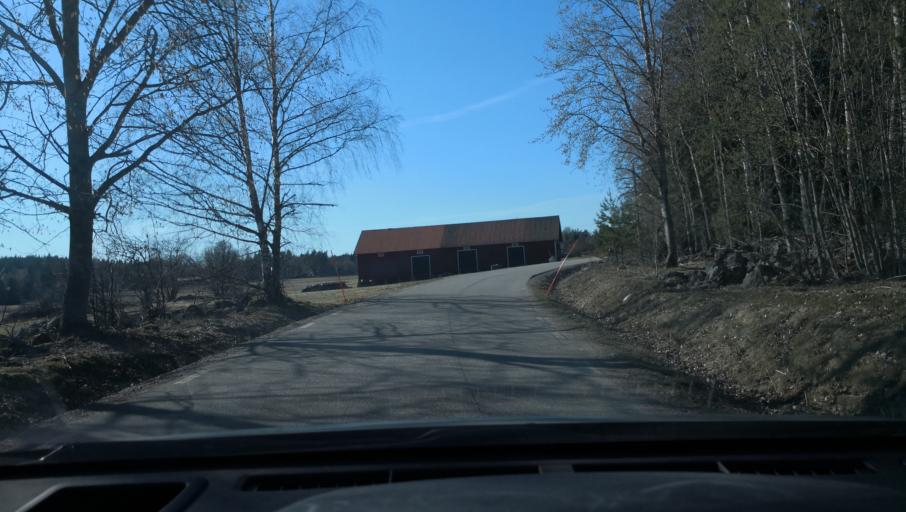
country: SE
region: Vaestmanland
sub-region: Sala Kommun
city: Sala
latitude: 60.0805
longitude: 16.4584
